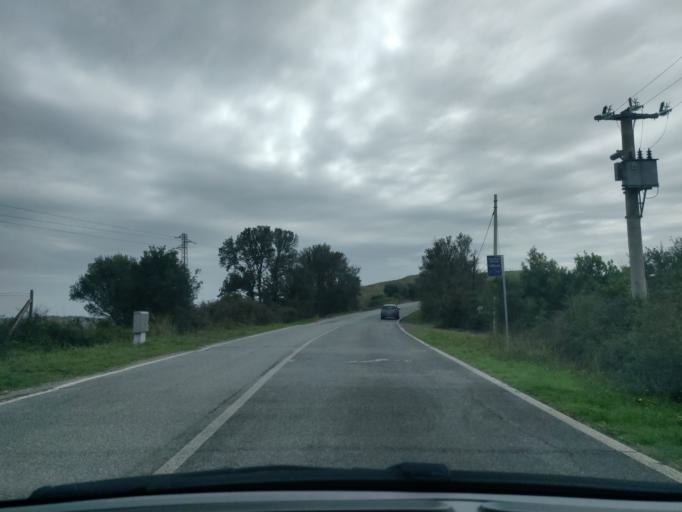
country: IT
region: Latium
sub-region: Citta metropolitana di Roma Capitale
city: Allumiere
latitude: 42.1181
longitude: 11.8616
